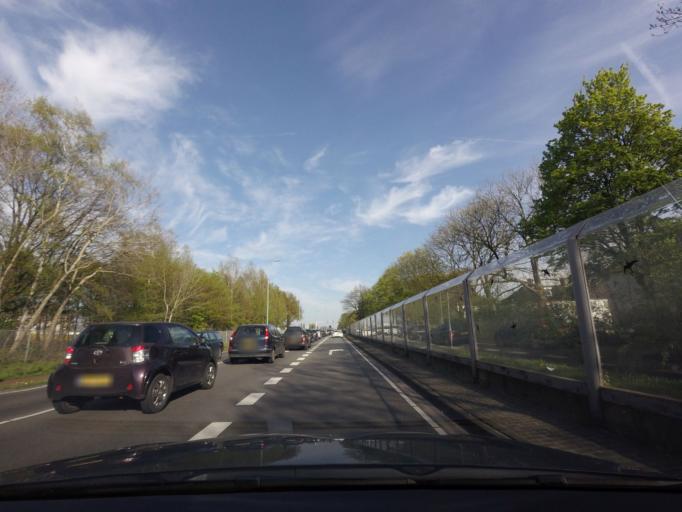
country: NL
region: North Brabant
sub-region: Gemeente Eindhoven
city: De Doornakkers
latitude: 51.4304
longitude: 5.5081
